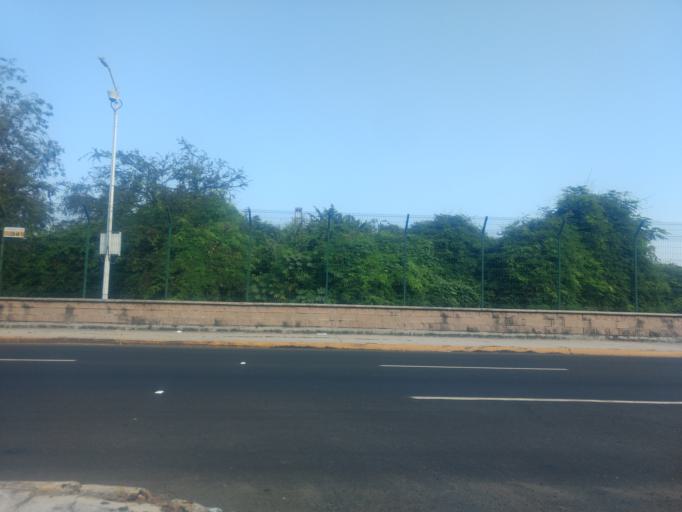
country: MX
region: Colima
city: Tapeixtles
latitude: 19.0685
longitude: -104.2862
